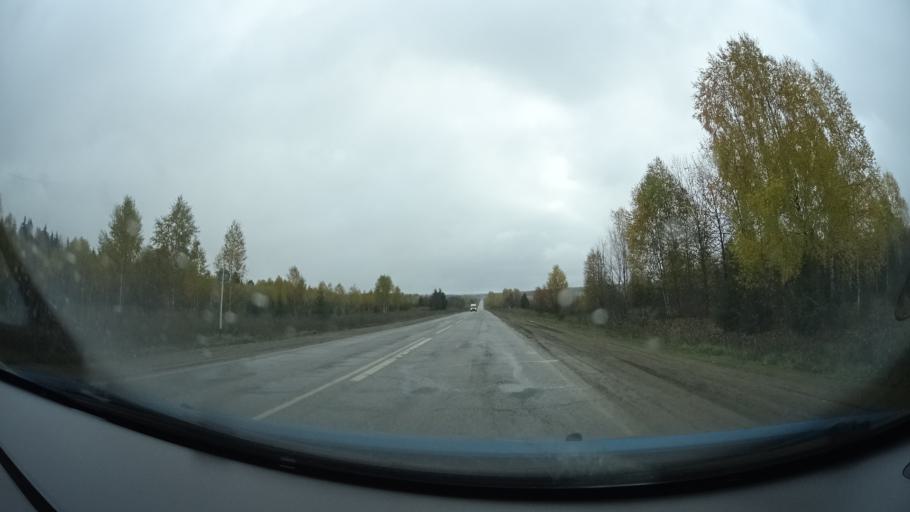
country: RU
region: Perm
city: Chernushka
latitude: 56.7544
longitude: 56.1473
